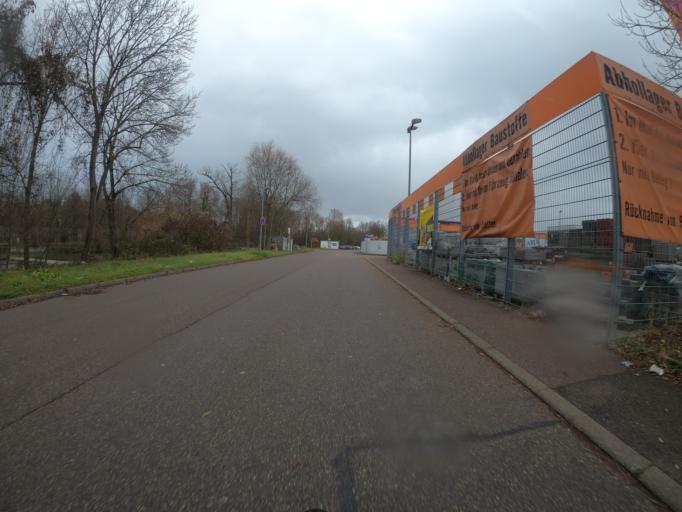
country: DE
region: Baden-Wuerttemberg
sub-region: Regierungsbezirk Stuttgart
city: Eislingen
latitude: 48.6994
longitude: 9.6801
